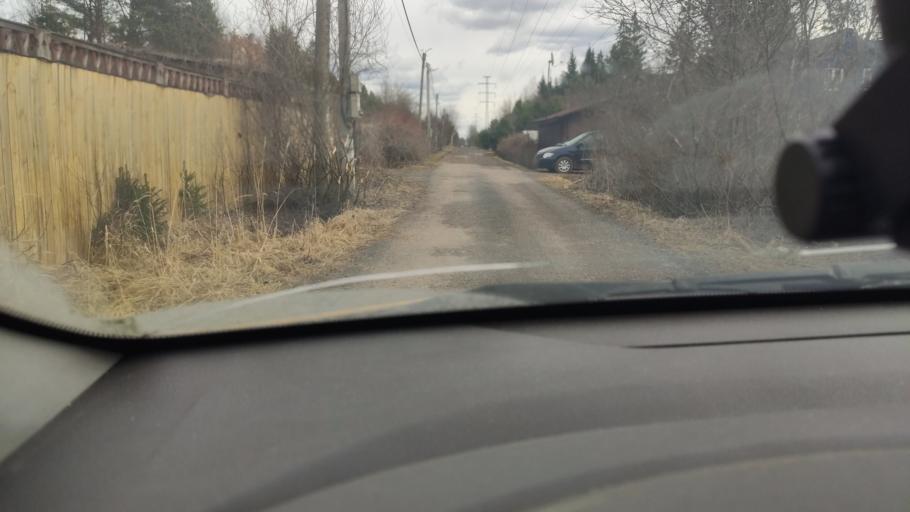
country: RU
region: Moskovskaya
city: Chupryakovo
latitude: 55.5830
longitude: 36.6004
